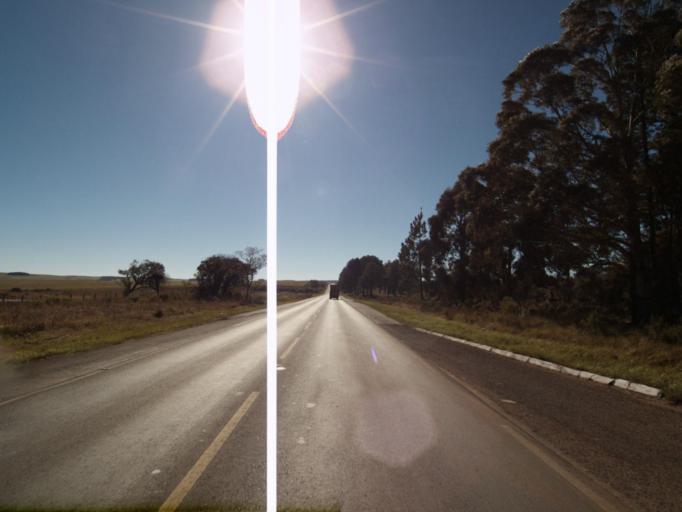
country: BR
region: Parana
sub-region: Palmas
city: Palmas
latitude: -26.7762
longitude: -51.6811
